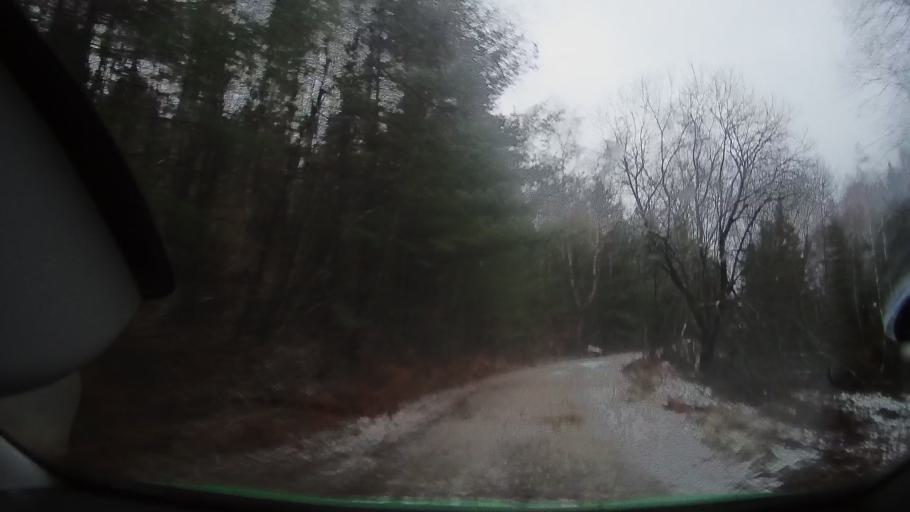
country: RO
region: Alba
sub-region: Comuna Avram Iancu
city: Avram Iancu
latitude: 46.3076
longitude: 22.7968
